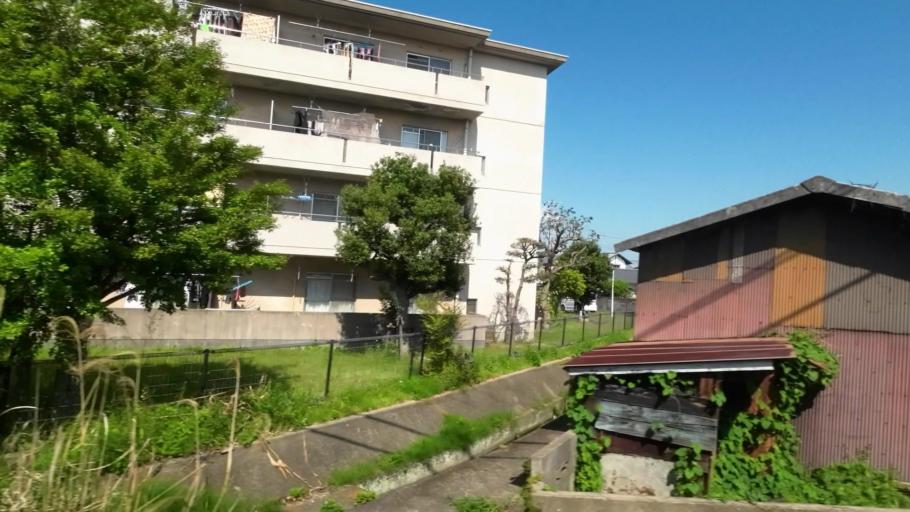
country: JP
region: Kagawa
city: Tadotsu
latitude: 34.2666
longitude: 133.7546
